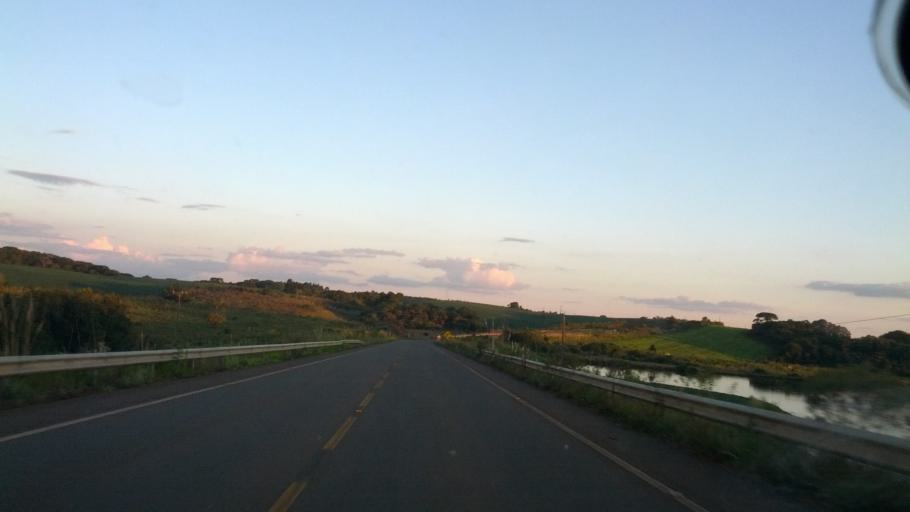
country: BR
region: Rio Grande do Sul
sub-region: Vacaria
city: Estrela
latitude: -27.8165
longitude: -50.8544
